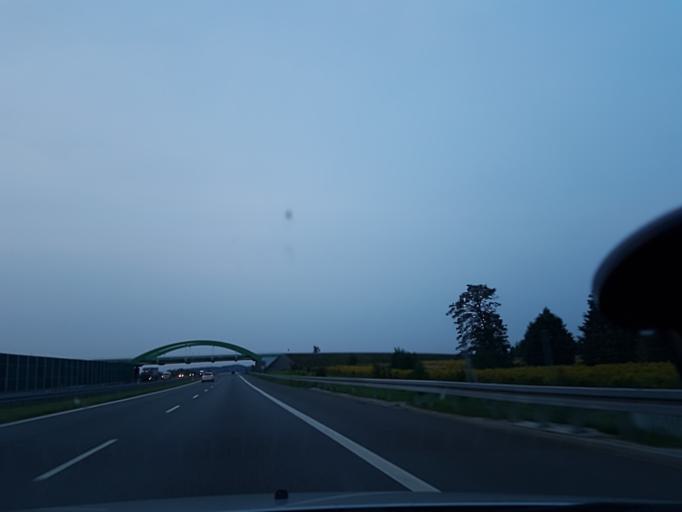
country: PL
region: Lodz Voivodeship
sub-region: Powiat zgierski
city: Strykow
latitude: 51.9143
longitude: 19.6218
